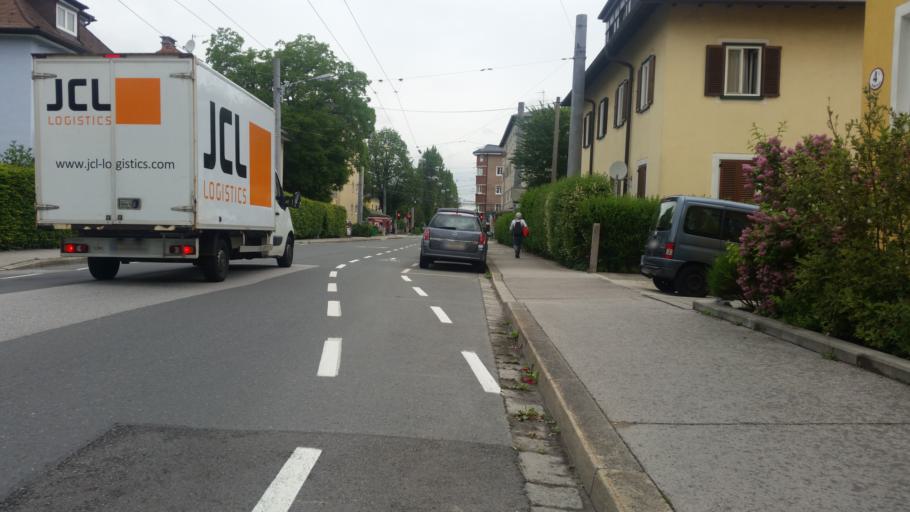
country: AT
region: Salzburg
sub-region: Salzburg Stadt
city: Salzburg
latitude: 47.8018
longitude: 13.0297
